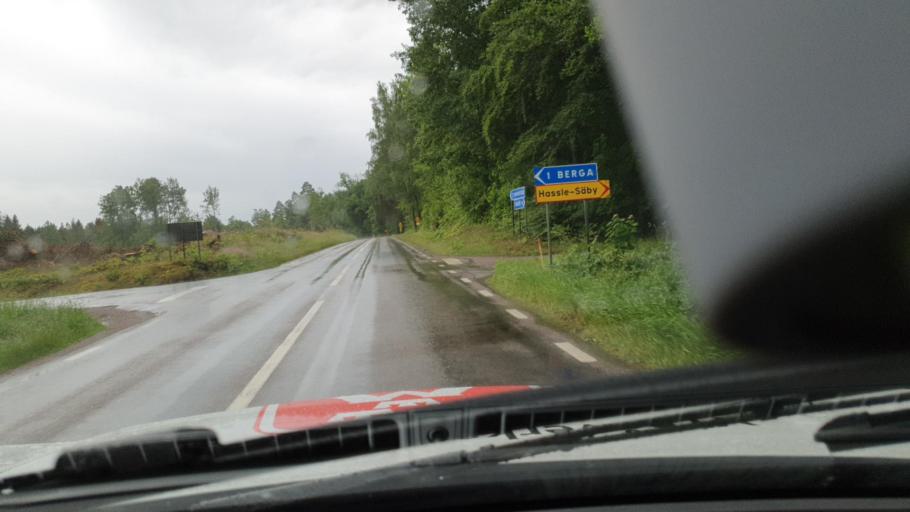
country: SE
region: Vaestra Goetaland
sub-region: Mariestads Kommun
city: Mariestad
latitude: 58.7440
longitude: 13.8997
